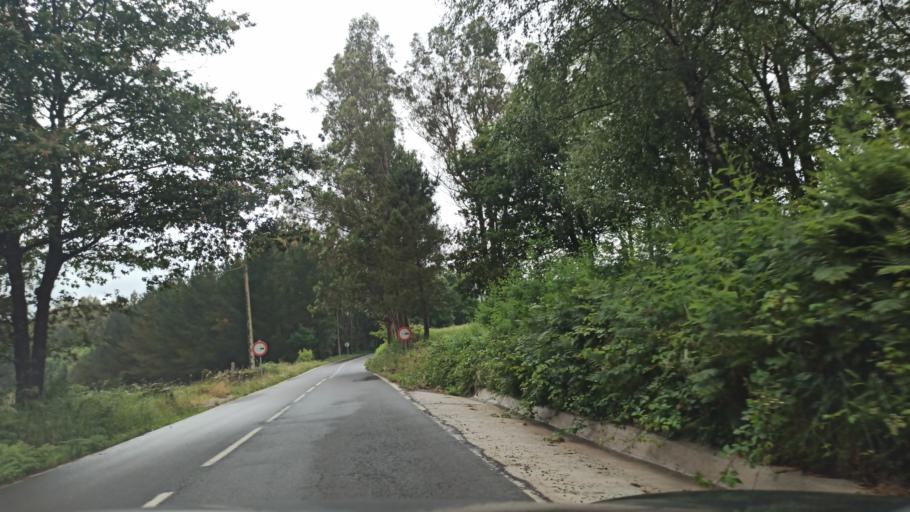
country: ES
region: Galicia
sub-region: Provincia da Coruna
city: Santiso
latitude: 42.7694
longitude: -8.0271
